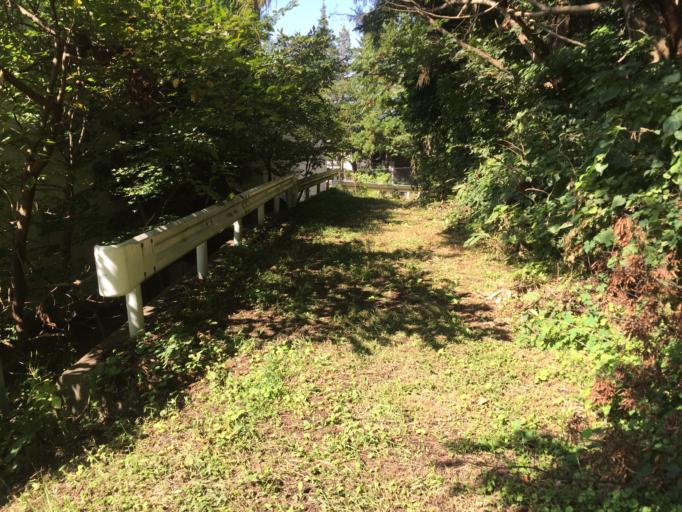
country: JP
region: Fukushima
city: Inawashiro
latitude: 37.4856
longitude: 139.9550
